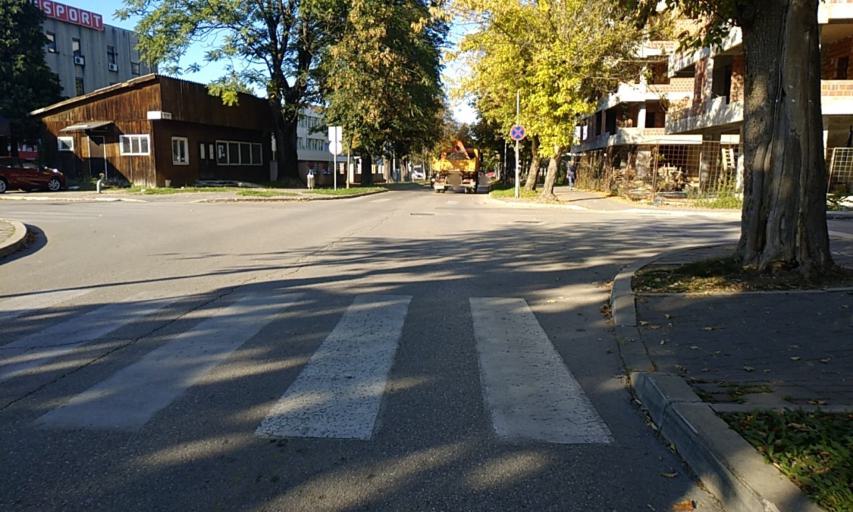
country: BA
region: Republika Srpska
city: Banja Luka
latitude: 44.7745
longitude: 17.1870
